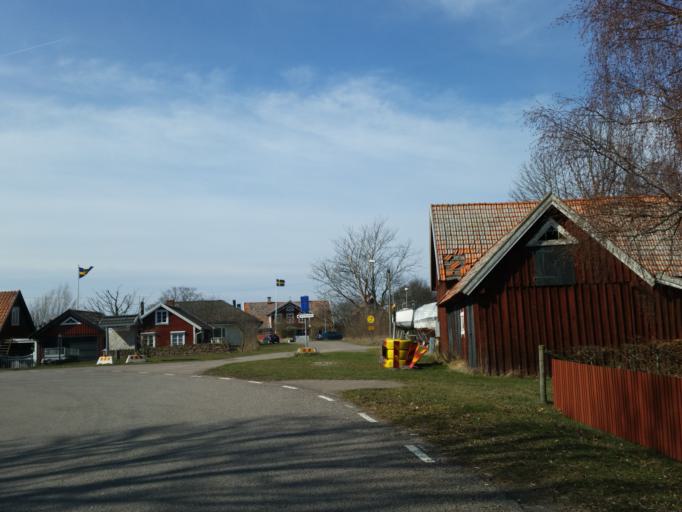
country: SE
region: Kalmar
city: Faerjestaden
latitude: 56.7568
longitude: 16.5297
